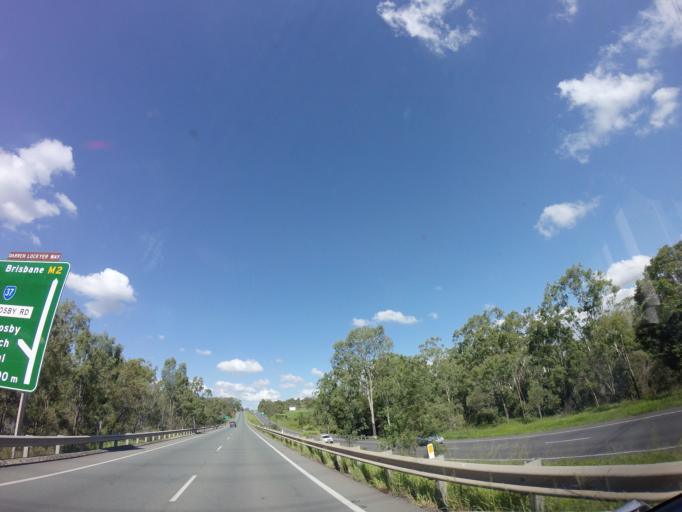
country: AU
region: Queensland
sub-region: Ipswich
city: Tivoli
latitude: -27.5775
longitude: 152.7787
